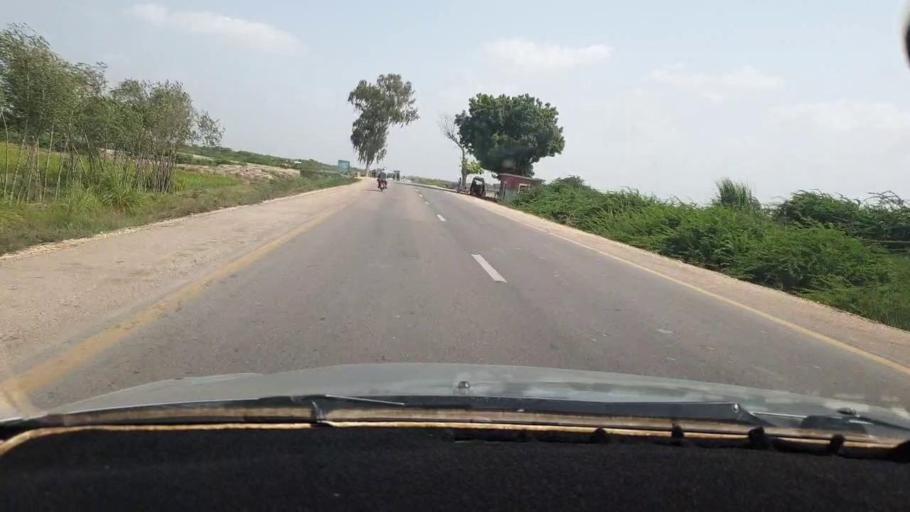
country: PK
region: Sindh
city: Digri
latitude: 25.1387
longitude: 69.1304
